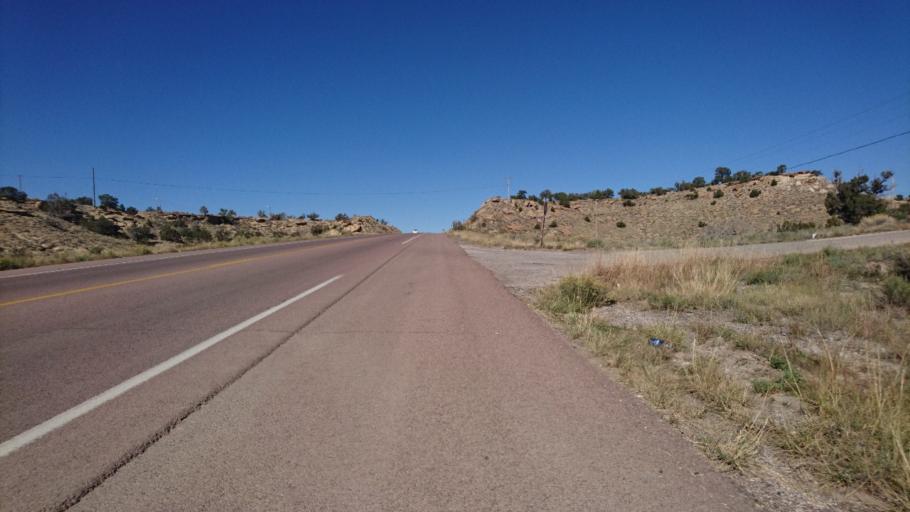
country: US
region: New Mexico
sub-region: McKinley County
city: Gallup
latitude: 35.4753
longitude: -108.7422
